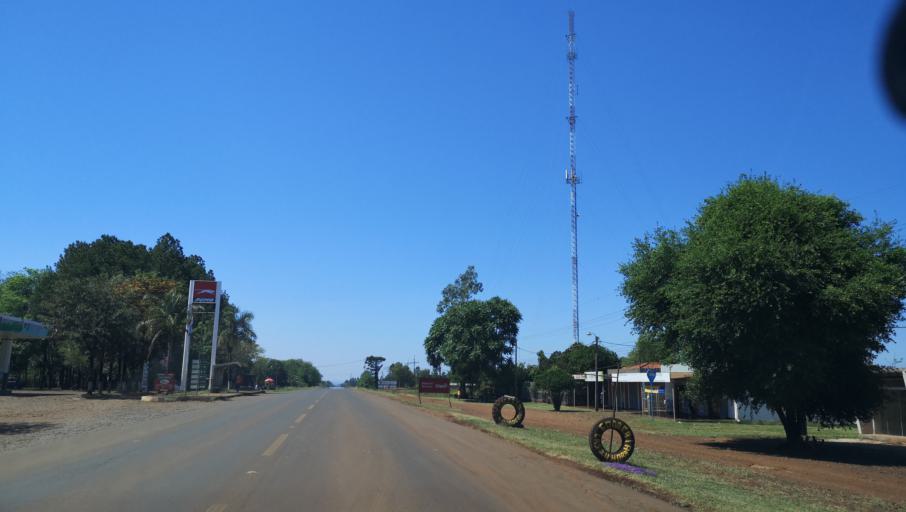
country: PY
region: Itapua
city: San Juan del Parana
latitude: -27.2651
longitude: -55.9609
